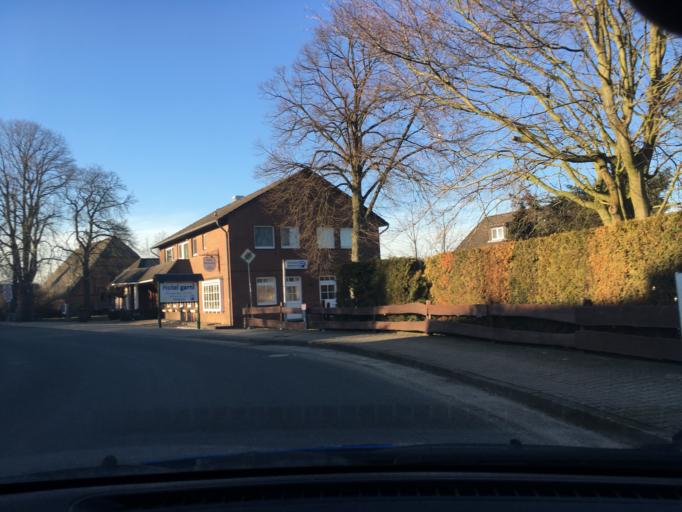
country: DE
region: Schleswig-Holstein
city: Mussen
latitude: 53.4931
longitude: 10.5650
